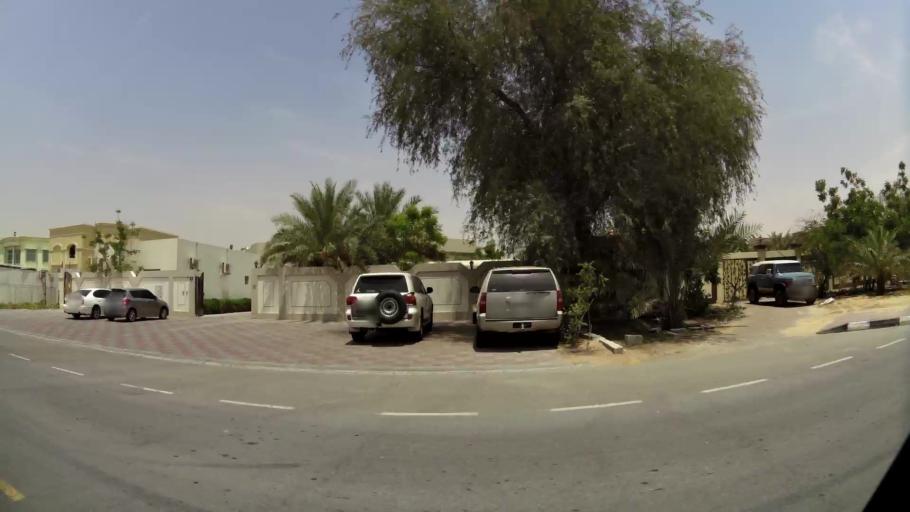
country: AE
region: Ash Shariqah
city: Sharjah
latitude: 25.1916
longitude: 55.3794
